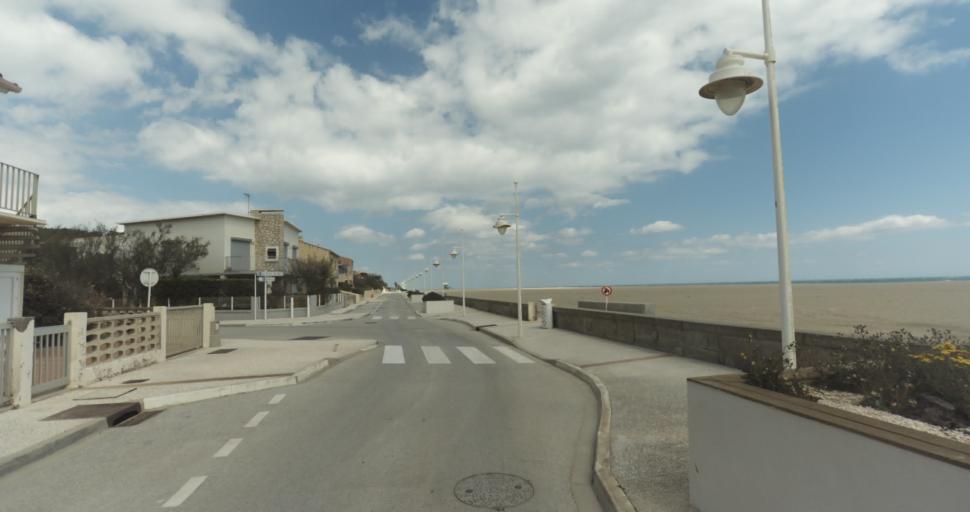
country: FR
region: Languedoc-Roussillon
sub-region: Departement de l'Aude
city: Leucate
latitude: 42.9023
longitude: 3.0545
